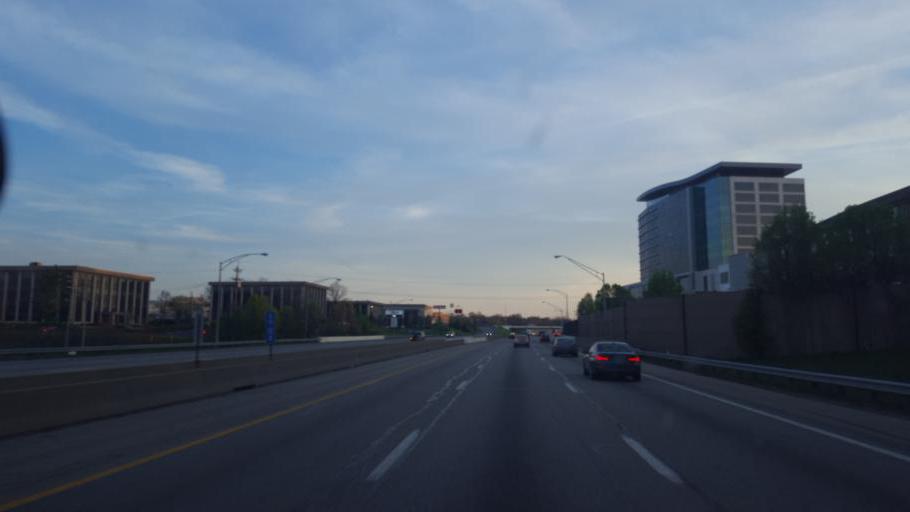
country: US
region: Ohio
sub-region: Hamilton County
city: Kenwood
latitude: 39.2067
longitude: -84.3719
